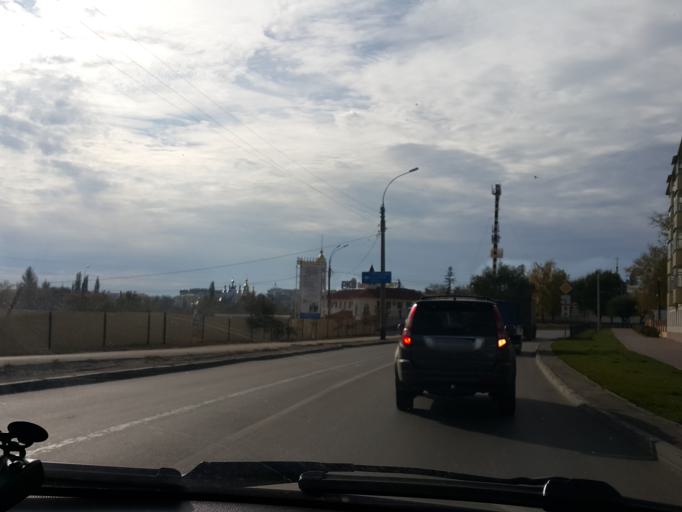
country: RU
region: Tambov
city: Tambov
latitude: 52.7293
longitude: 41.4630
